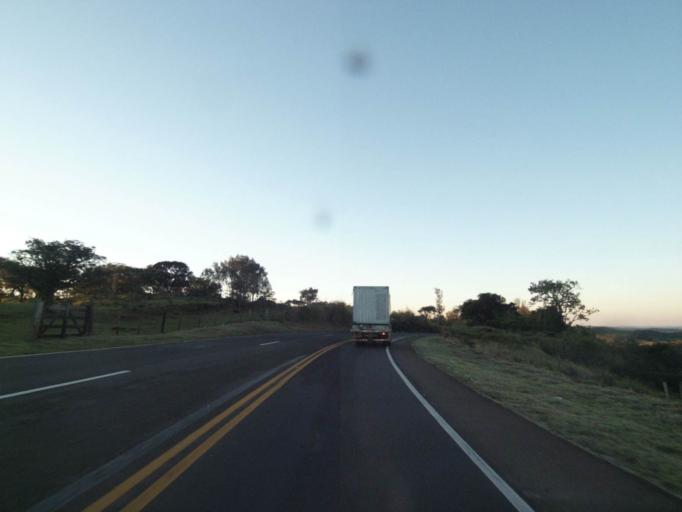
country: BR
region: Parana
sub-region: Londrina
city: Londrina
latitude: -23.4898
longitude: -51.1339
